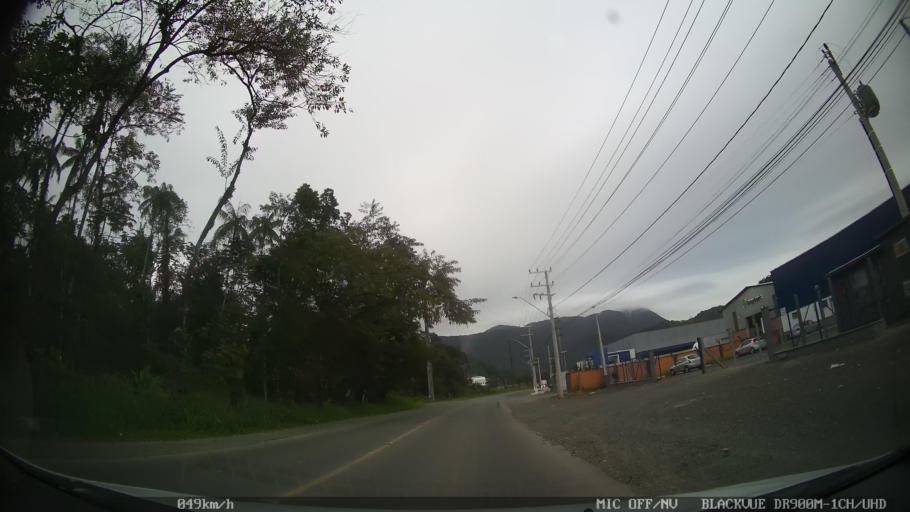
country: BR
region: Santa Catarina
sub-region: Joinville
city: Joinville
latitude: -26.2319
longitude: -48.9071
